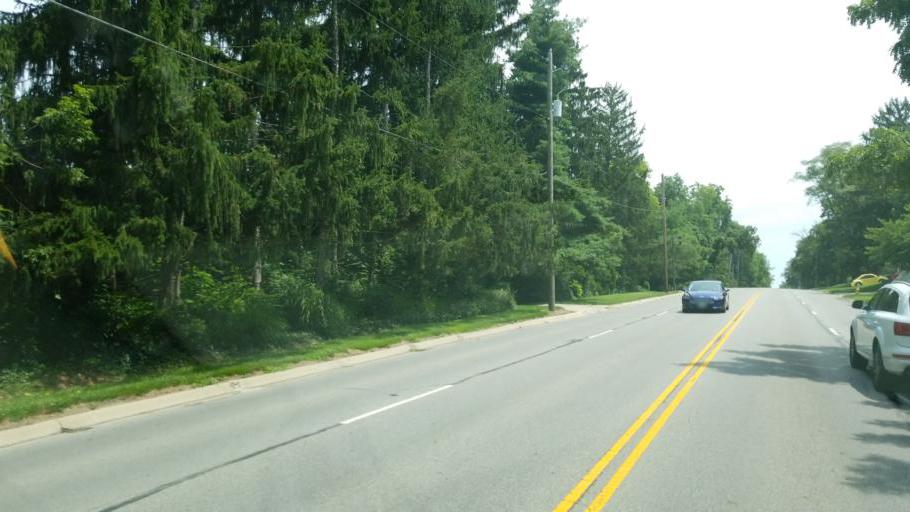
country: US
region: Ohio
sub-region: Franklin County
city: Upper Arlington
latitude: 40.0298
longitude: -83.0830
